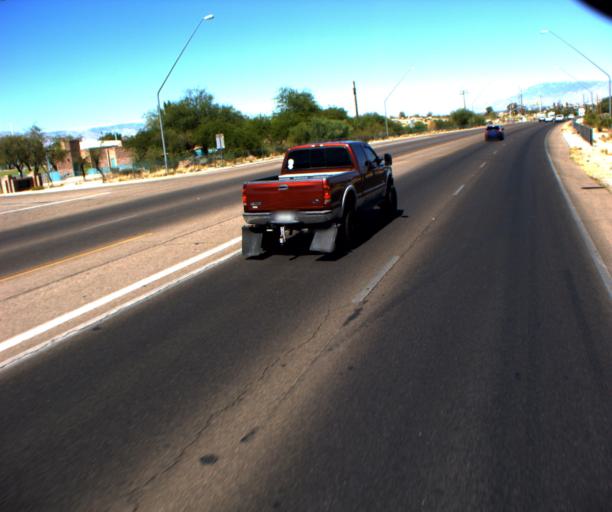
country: US
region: Arizona
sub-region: Pima County
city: Drexel Heights
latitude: 32.1777
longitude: -111.0144
